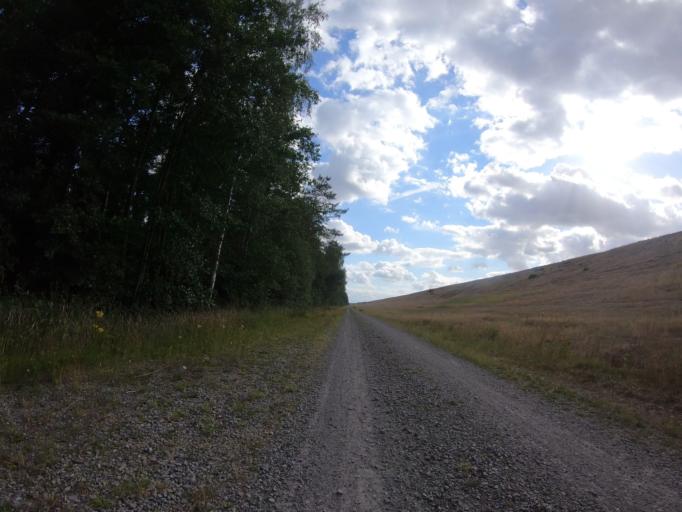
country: DE
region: Lower Saxony
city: Osloss
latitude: 52.4586
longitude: 10.6442
